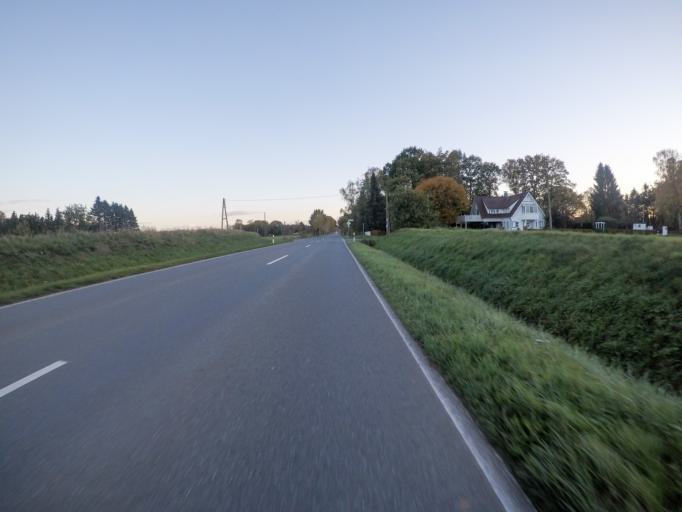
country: DE
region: North Rhine-Westphalia
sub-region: Regierungsbezirk Munster
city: Isselburg
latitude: 51.8511
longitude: 6.4745
